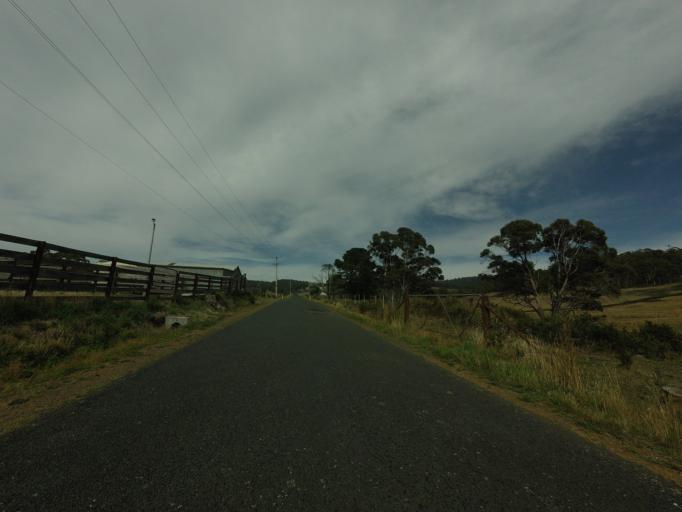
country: AU
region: Tasmania
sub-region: Sorell
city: Sorell
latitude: -42.4626
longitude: 147.5720
